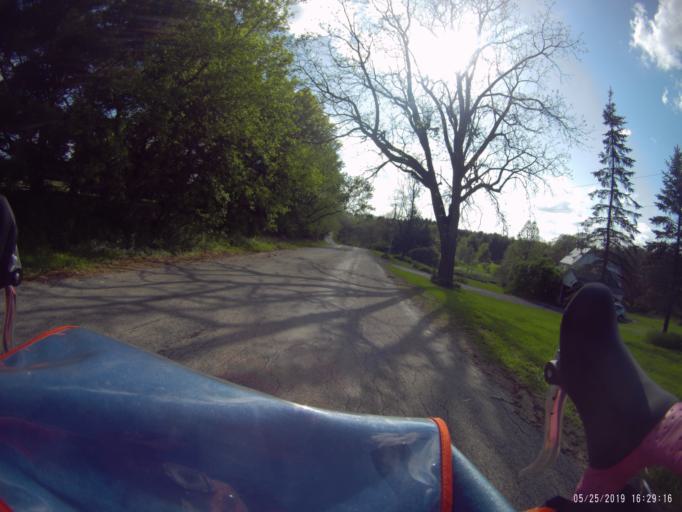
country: US
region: Wisconsin
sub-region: Dane County
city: Mount Horeb
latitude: 42.9454
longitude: -89.7123
